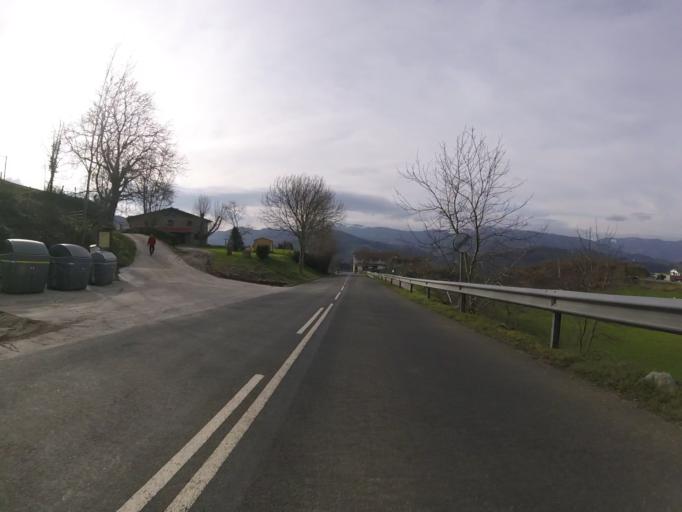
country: ES
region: Basque Country
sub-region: Provincia de Guipuzcoa
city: Azpeitia
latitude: 43.1668
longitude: -2.2273
